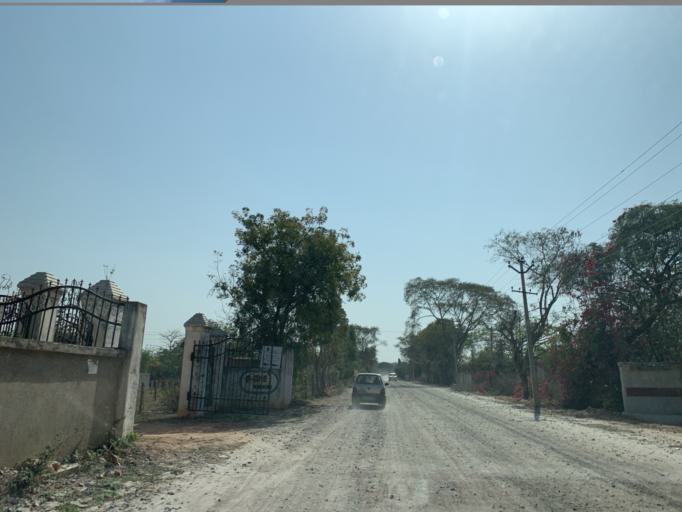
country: IN
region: Telangana
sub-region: Rangareddi
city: Sriramnagar
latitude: 17.3268
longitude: 78.2947
